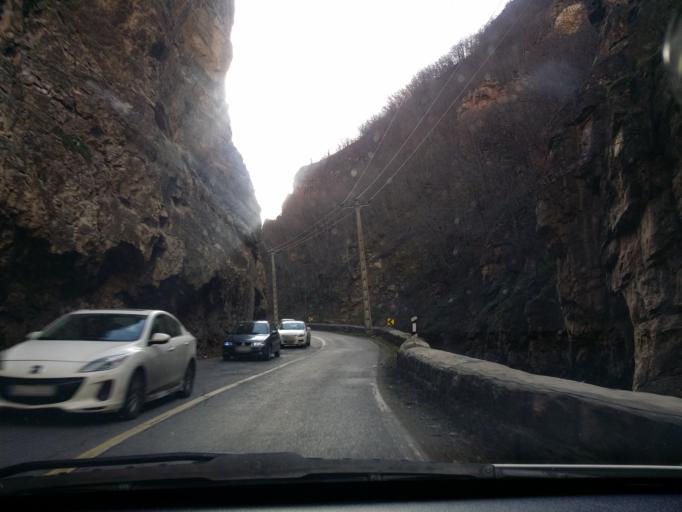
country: IR
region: Mazandaran
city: Chalus
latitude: 36.2698
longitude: 51.2488
